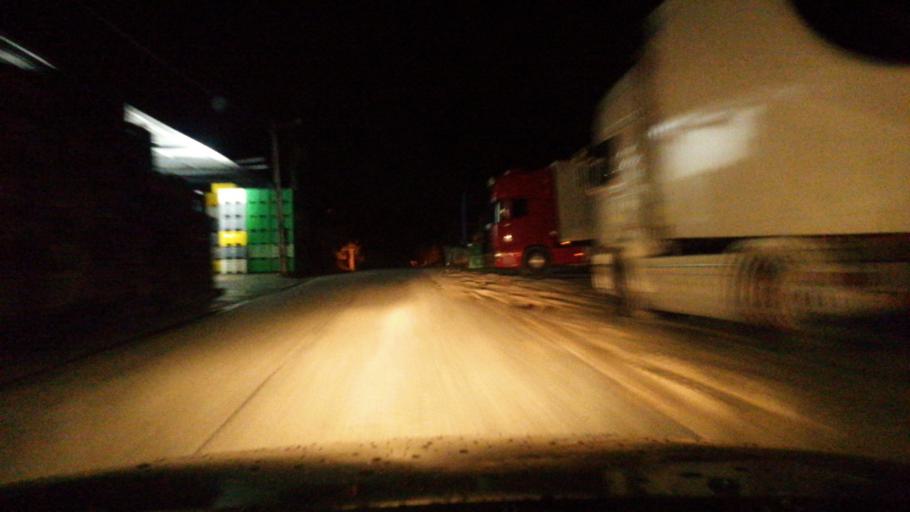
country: PT
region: Viseu
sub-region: Moimenta da Beira
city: Moimenta da Beira
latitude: 41.0451
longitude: -7.6405
